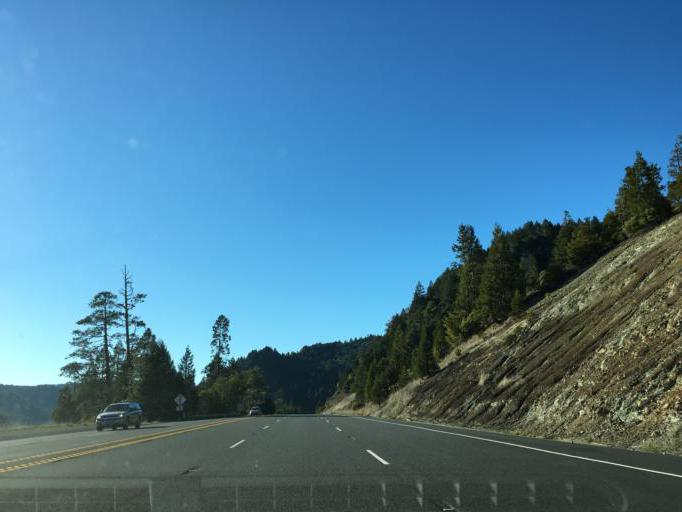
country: US
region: California
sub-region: Mendocino County
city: Laytonville
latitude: 39.8342
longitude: -123.6368
